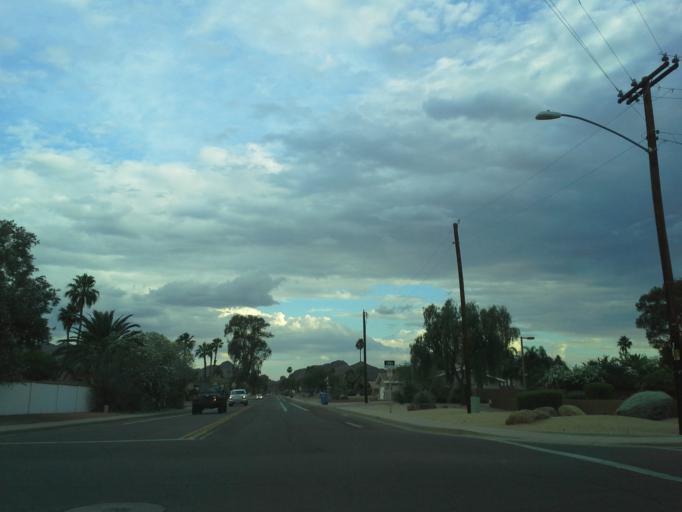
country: US
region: Arizona
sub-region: Maricopa County
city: Paradise Valley
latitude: 33.5899
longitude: -112.0045
